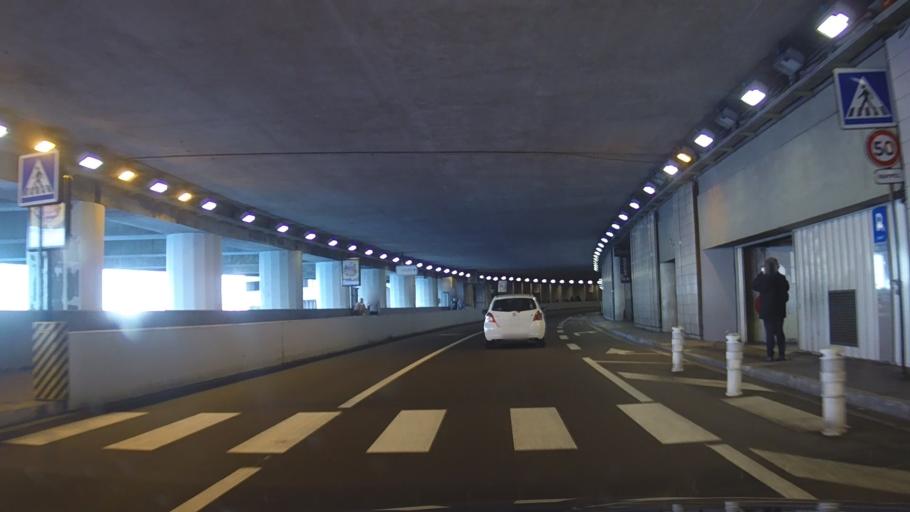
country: MC
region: Commune de Monaco
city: Monte-Carlo
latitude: 43.7394
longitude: 7.4301
